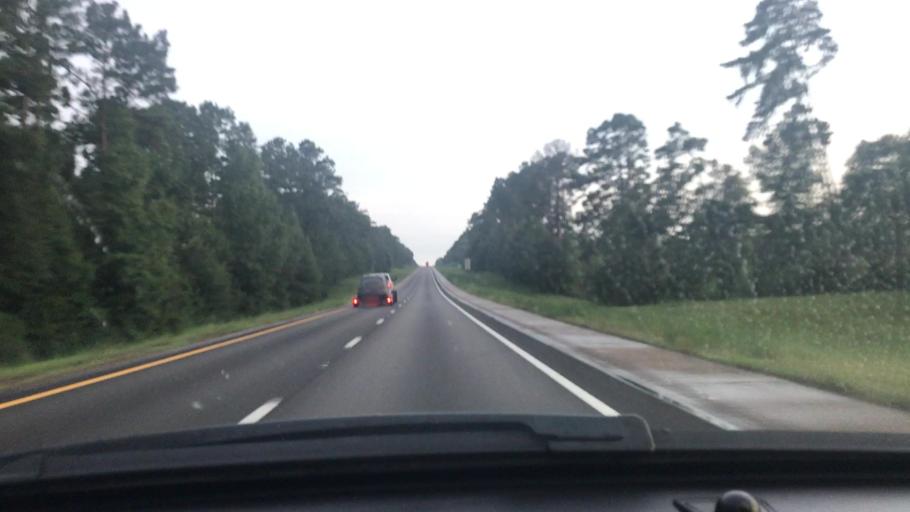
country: US
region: Mississippi
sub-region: Pike County
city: Magnolia
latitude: 31.0570
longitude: -90.4947
